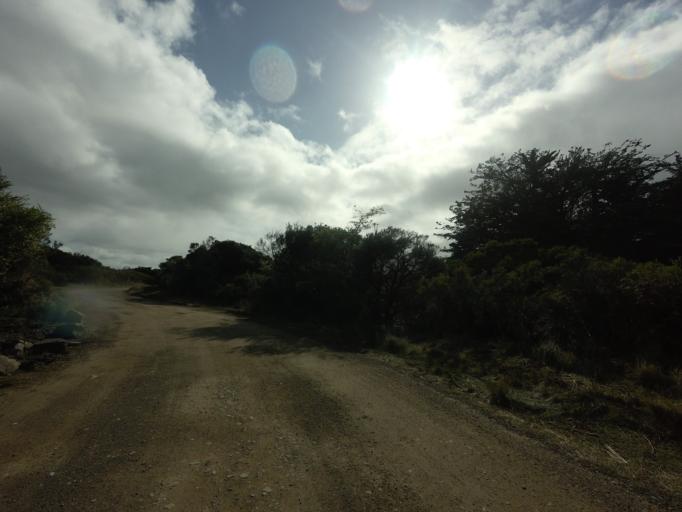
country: AU
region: Tasmania
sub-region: Huon Valley
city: Geeveston
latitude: -43.5819
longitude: 146.8970
